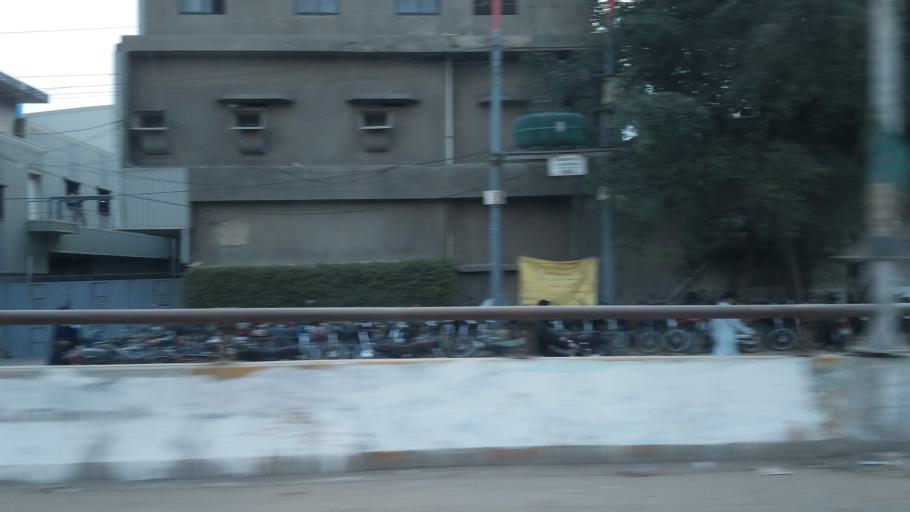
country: PK
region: Sindh
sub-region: Karachi District
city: Karachi
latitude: 24.9413
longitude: 67.0850
